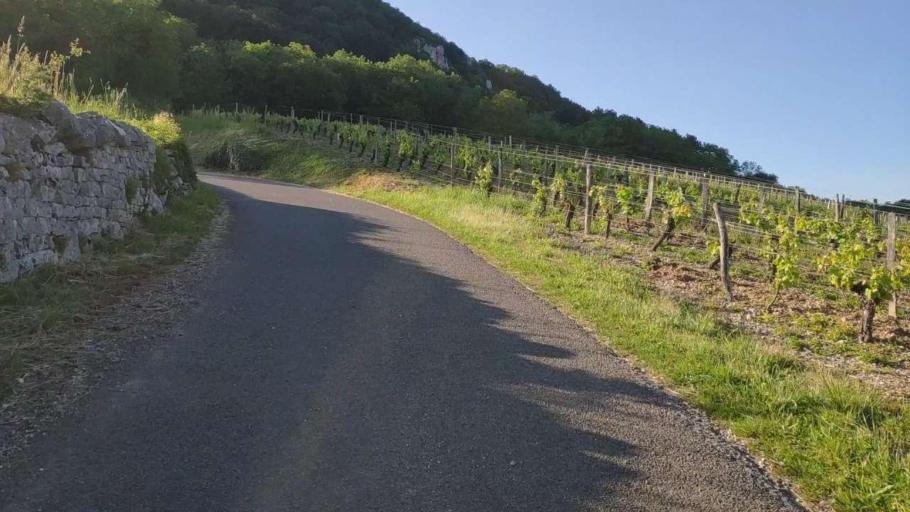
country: FR
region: Franche-Comte
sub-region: Departement du Jura
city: Perrigny
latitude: 46.7138
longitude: 5.5975
